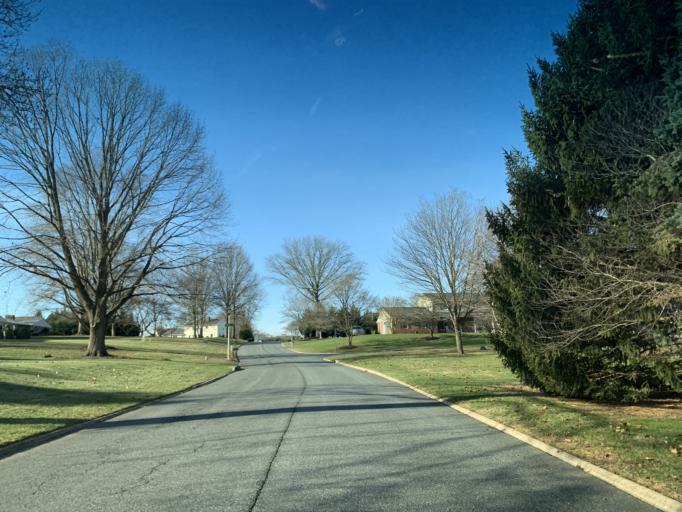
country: US
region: Maryland
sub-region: Harford County
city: South Bel Air
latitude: 39.5684
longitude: -76.2647
